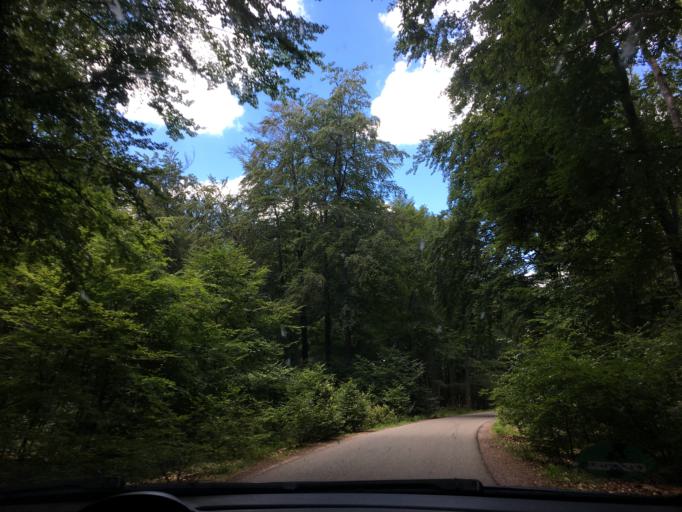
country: DE
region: Rheinland-Pfalz
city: Leimen
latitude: 49.2622
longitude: 7.8271
